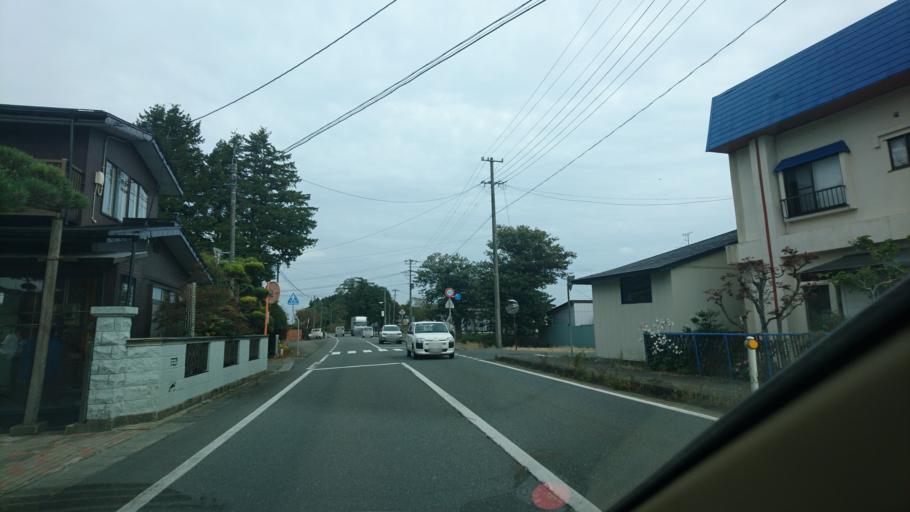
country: JP
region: Iwate
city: Morioka-shi
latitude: 39.6143
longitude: 141.1148
